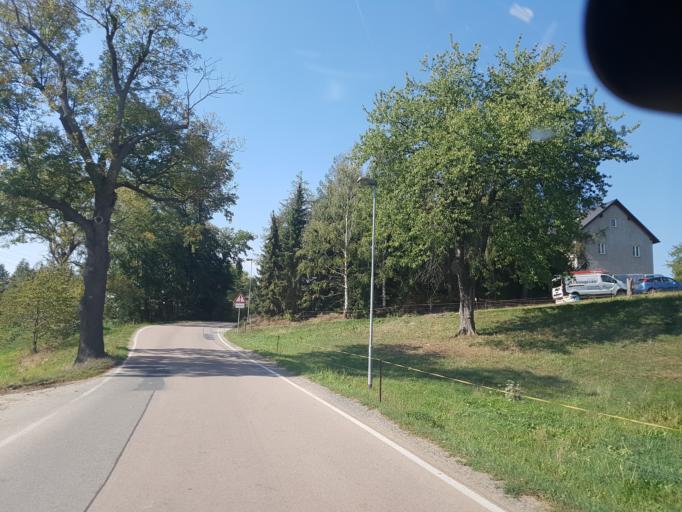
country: DE
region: Saxony
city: Kriebstein
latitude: 51.0578
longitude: 12.9878
